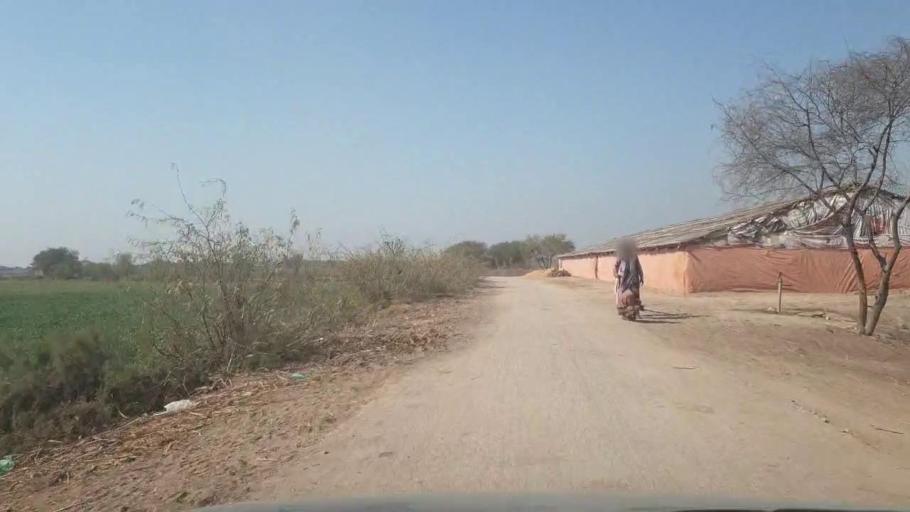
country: PK
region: Sindh
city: Chambar
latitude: 25.3657
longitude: 68.7664
